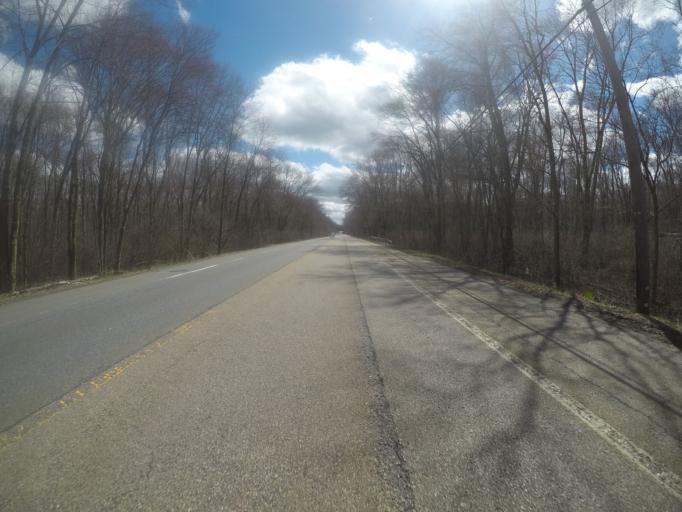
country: US
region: Massachusetts
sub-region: Bristol County
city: Raynham
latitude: 41.9914
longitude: -71.0693
